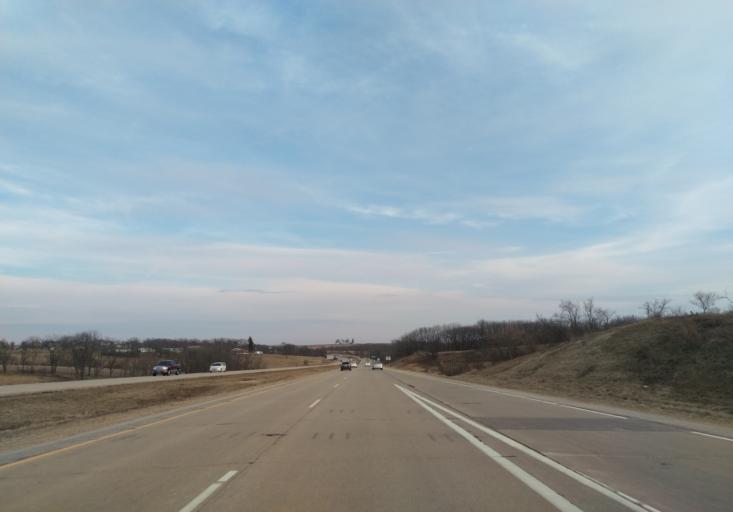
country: US
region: Wisconsin
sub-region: Dane County
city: Mount Horeb
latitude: 42.9979
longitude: -89.7536
